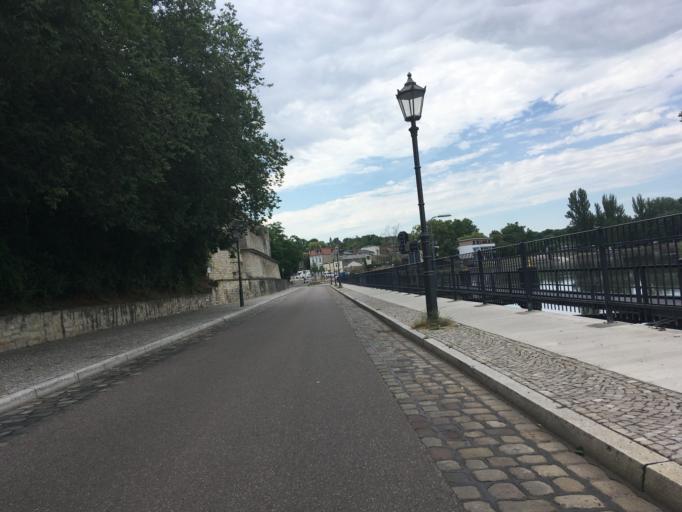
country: DE
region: Saxony-Anhalt
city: Bernburg
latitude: 51.7949
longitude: 11.7335
